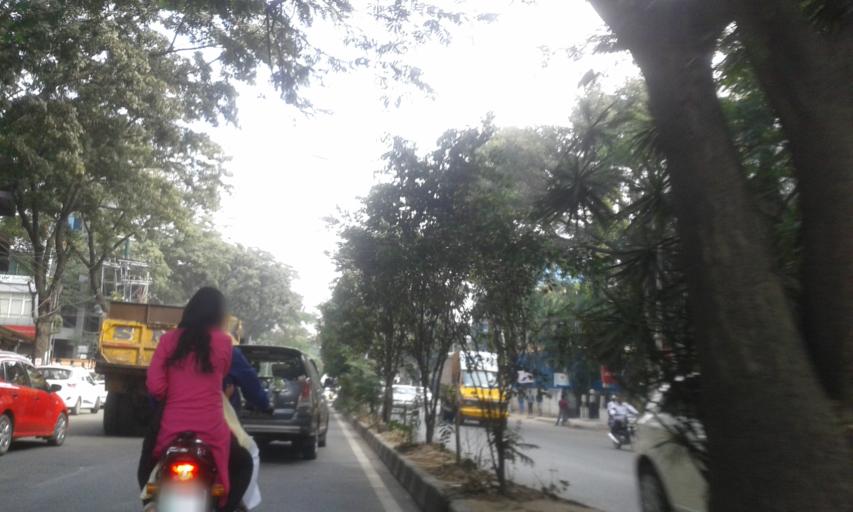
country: IN
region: Karnataka
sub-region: Bangalore Urban
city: Bangalore
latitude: 12.9329
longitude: 77.6231
